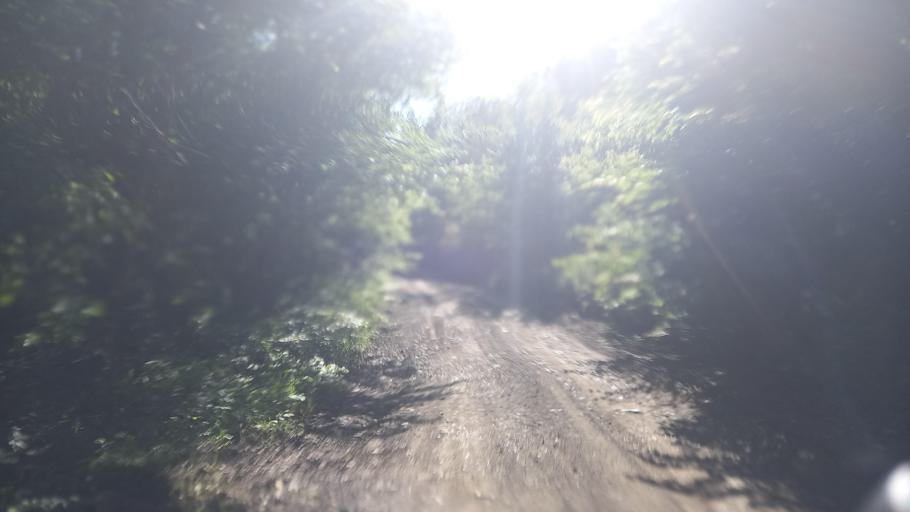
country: RU
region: Krasnodarskiy
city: Dzhubga
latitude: 44.5356
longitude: 38.7630
